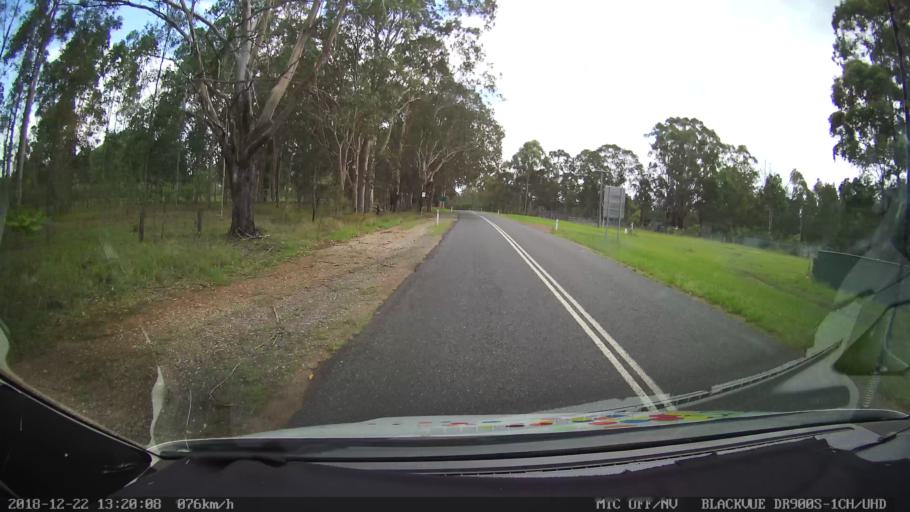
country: AU
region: New South Wales
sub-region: Clarence Valley
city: South Grafton
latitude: -29.7631
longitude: 152.9289
